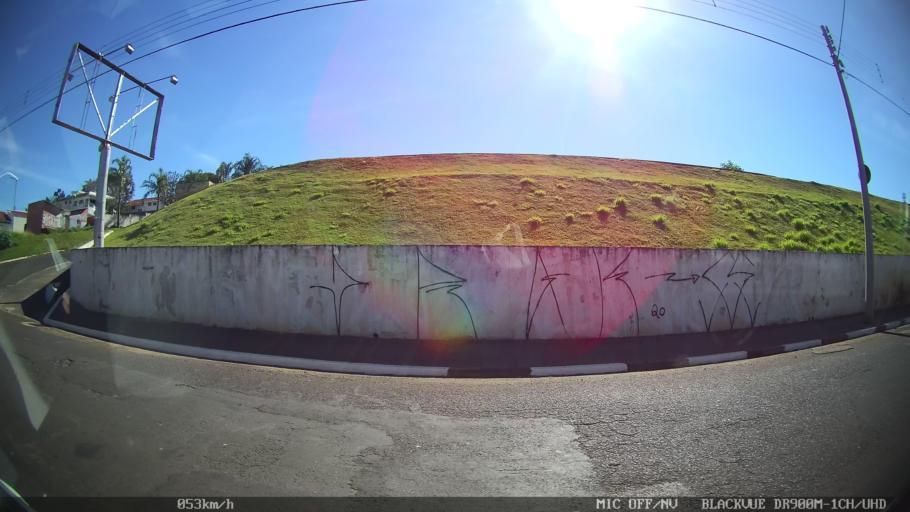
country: BR
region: Sao Paulo
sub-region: Franca
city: Franca
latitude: -20.5197
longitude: -47.3849
